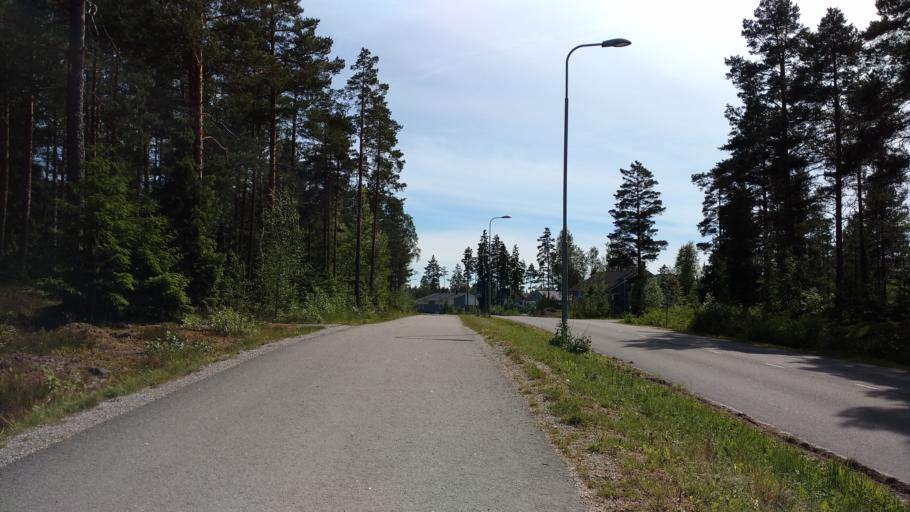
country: FI
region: Varsinais-Suomi
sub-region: Salo
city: Salo
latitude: 60.4005
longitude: 23.1914
